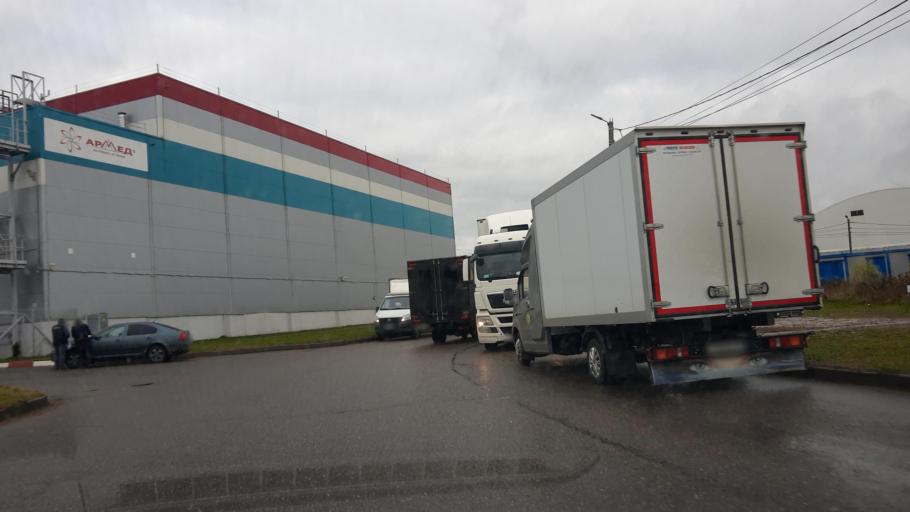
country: RU
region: Moskovskaya
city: Mosrentgen
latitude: 55.6012
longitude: 37.4539
